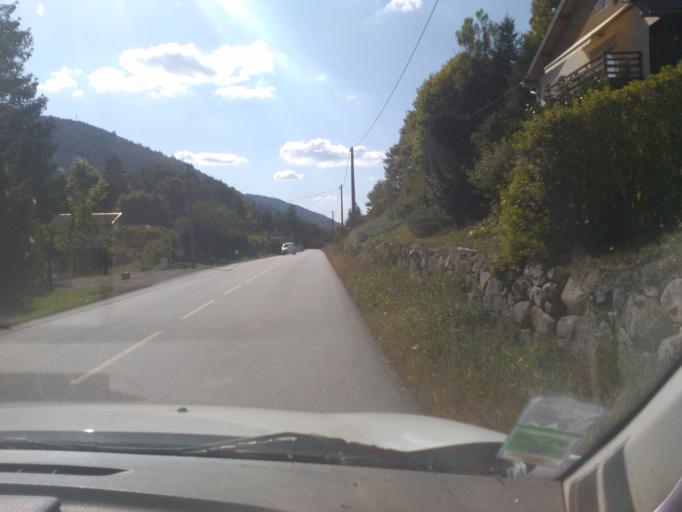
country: FR
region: Lorraine
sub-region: Departement des Vosges
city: La Bresse
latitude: 48.0311
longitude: 6.8242
